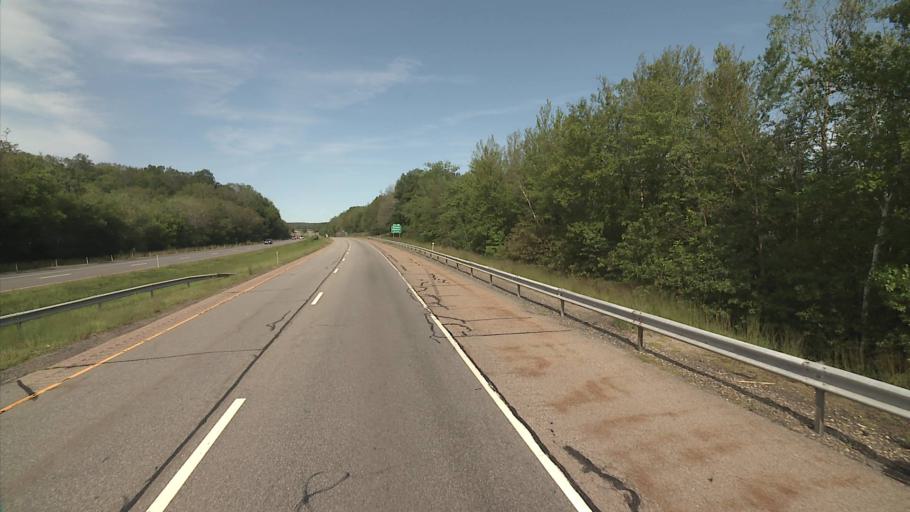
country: US
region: Connecticut
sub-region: New London County
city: Montville Center
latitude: 41.5720
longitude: -72.1928
